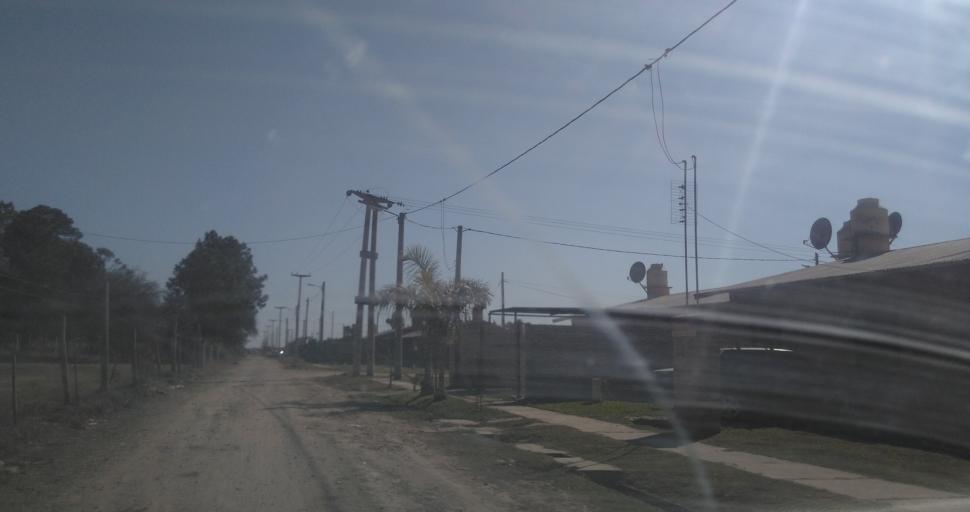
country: AR
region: Chaco
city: Fontana
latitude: -27.4532
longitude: -59.0381
